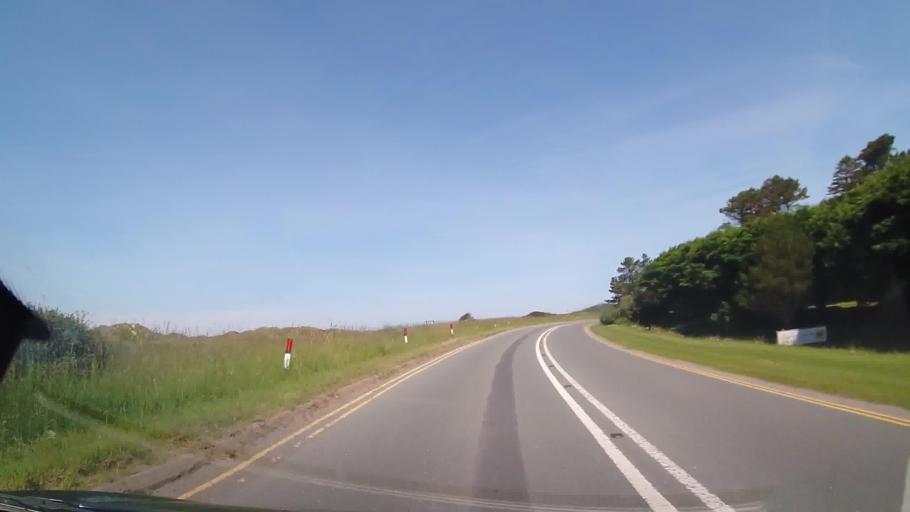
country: GB
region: Wales
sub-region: Gwynedd
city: Tywyn
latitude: 52.5459
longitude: -4.0680
